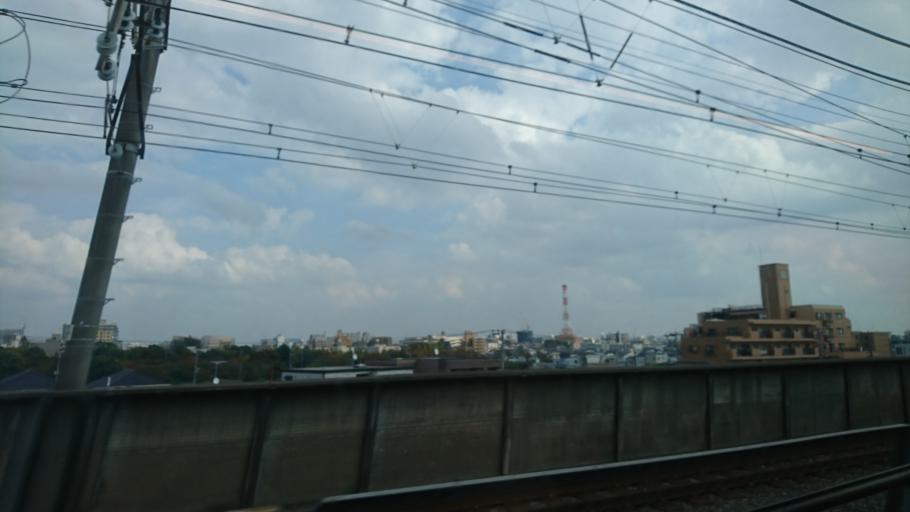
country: JP
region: Saitama
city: Yono
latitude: 35.8768
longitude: 139.6279
